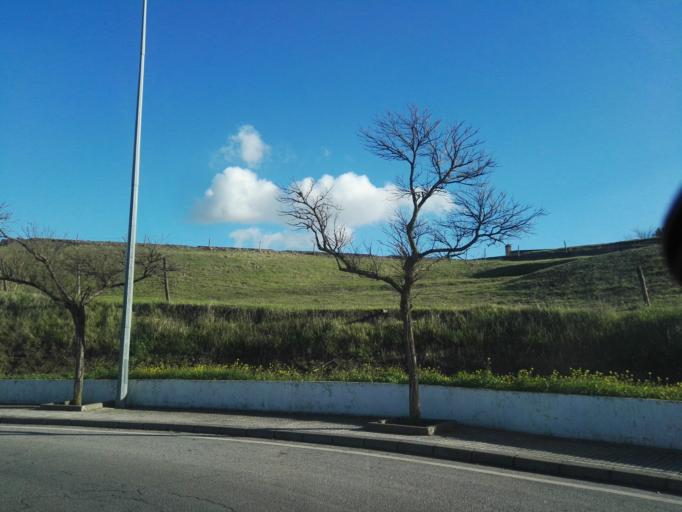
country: PT
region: Portalegre
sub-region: Elvas
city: Elvas
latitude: 38.8831
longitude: -7.1586
